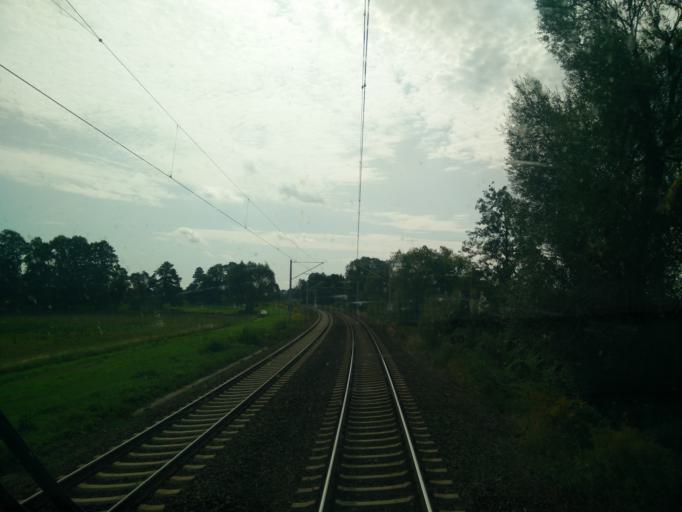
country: DE
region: Brandenburg
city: Lubbenau
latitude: 51.8782
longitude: 13.9190
